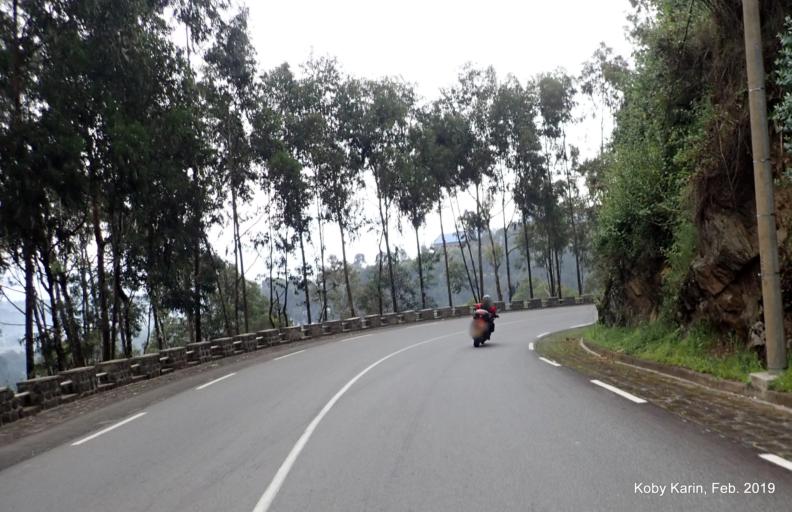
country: RW
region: Northern Province
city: Musanze
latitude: -1.5366
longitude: 29.5649
